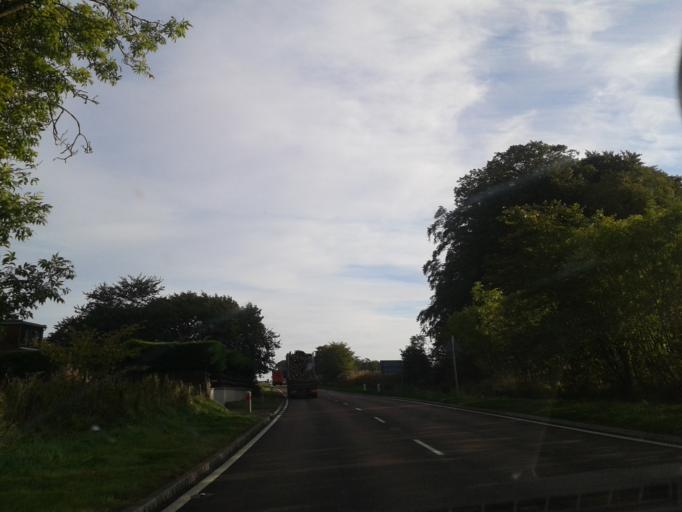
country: GB
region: Scotland
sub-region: Highland
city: Inverness
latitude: 57.4958
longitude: -4.1523
